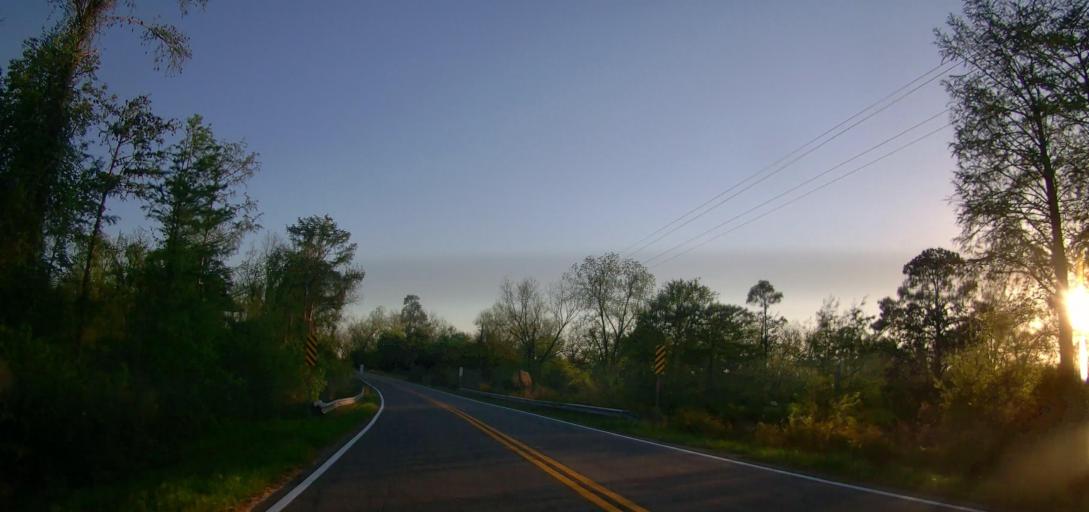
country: US
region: Georgia
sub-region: Irwin County
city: Ocilla
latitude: 31.6394
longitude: -83.2743
